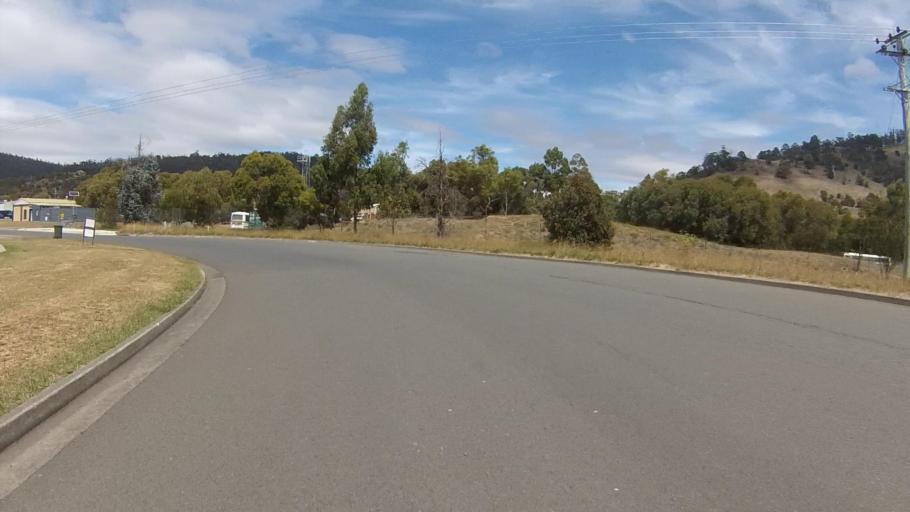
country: AU
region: Tasmania
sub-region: Clarence
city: Cambridge
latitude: -42.8330
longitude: 147.4485
